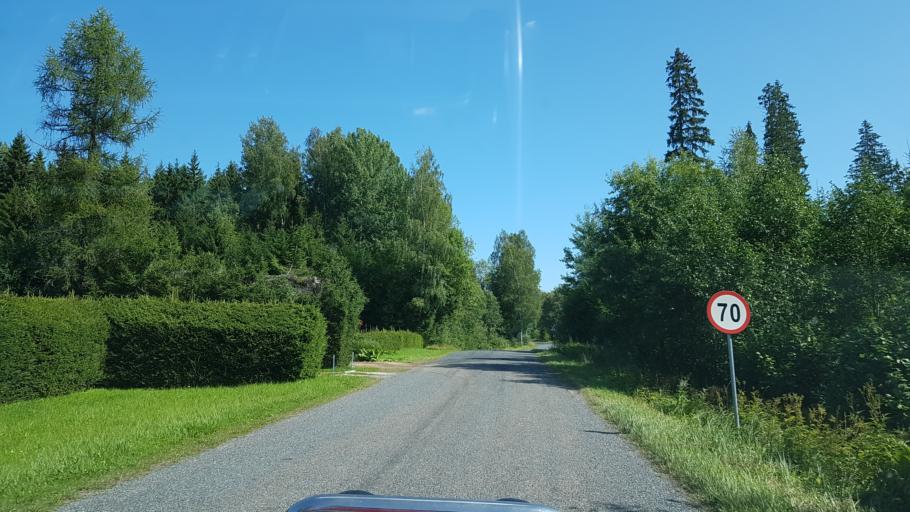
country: EE
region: Vorumaa
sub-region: Voru linn
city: Voru
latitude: 57.7506
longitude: 27.2794
